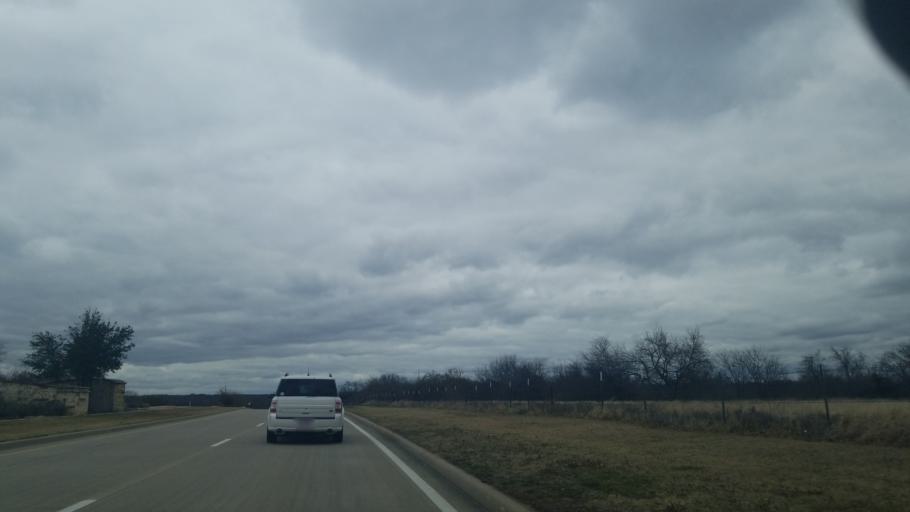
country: US
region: Texas
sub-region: Denton County
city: Copper Canyon
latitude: 33.1141
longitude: -97.0788
